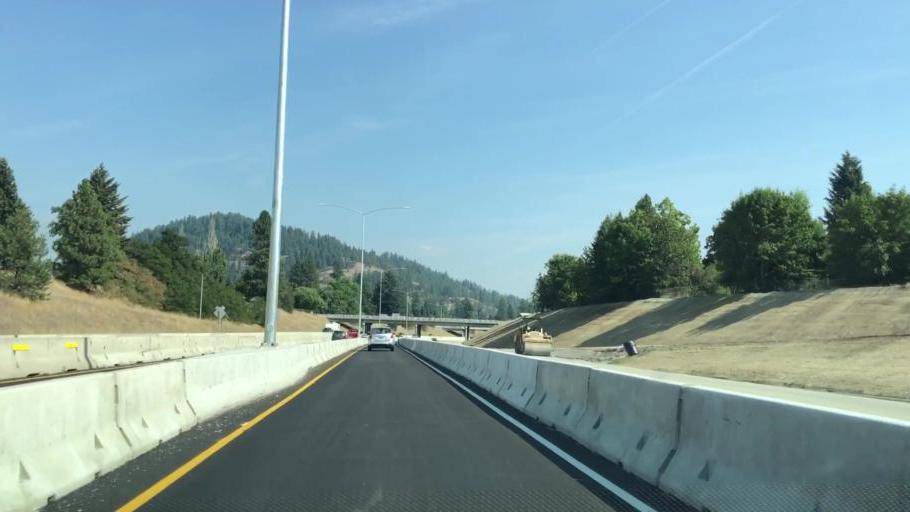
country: US
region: Idaho
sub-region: Kootenai County
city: Coeur d'Alene
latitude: 47.6973
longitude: -116.7796
